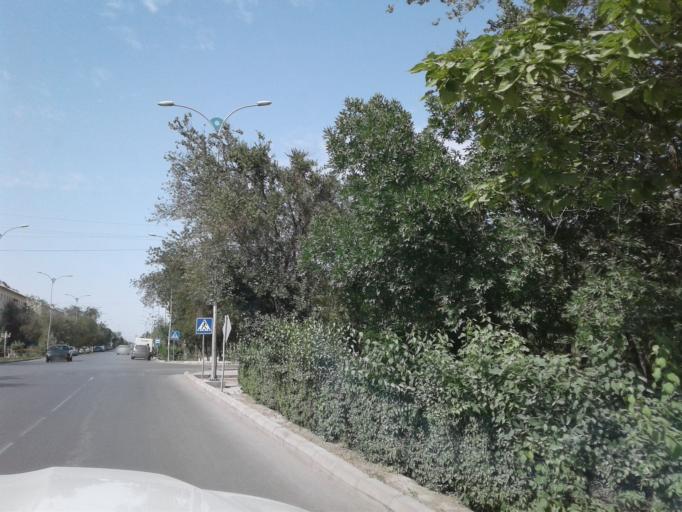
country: TM
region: Dasoguz
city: Dasoguz
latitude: 41.8315
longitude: 59.9458
